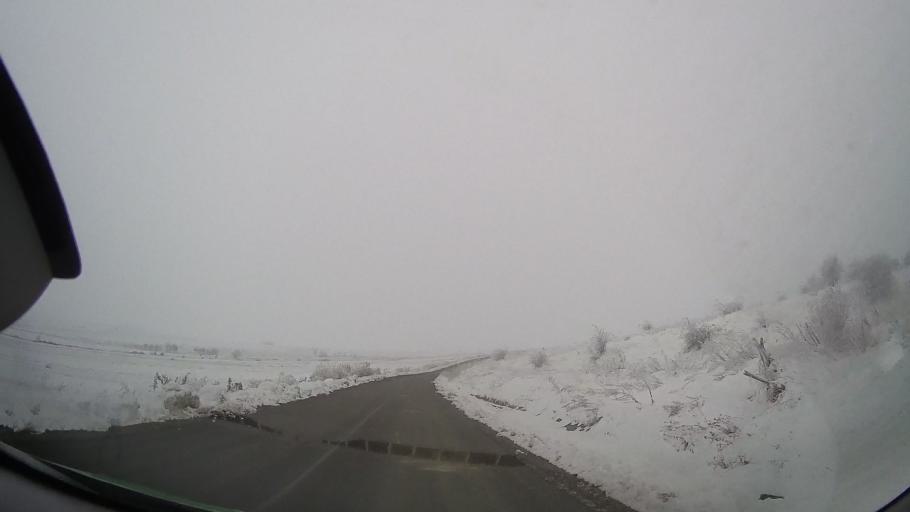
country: RO
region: Iasi
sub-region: Comuna Tansa
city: Suhulet
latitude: 46.8869
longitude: 27.2768
